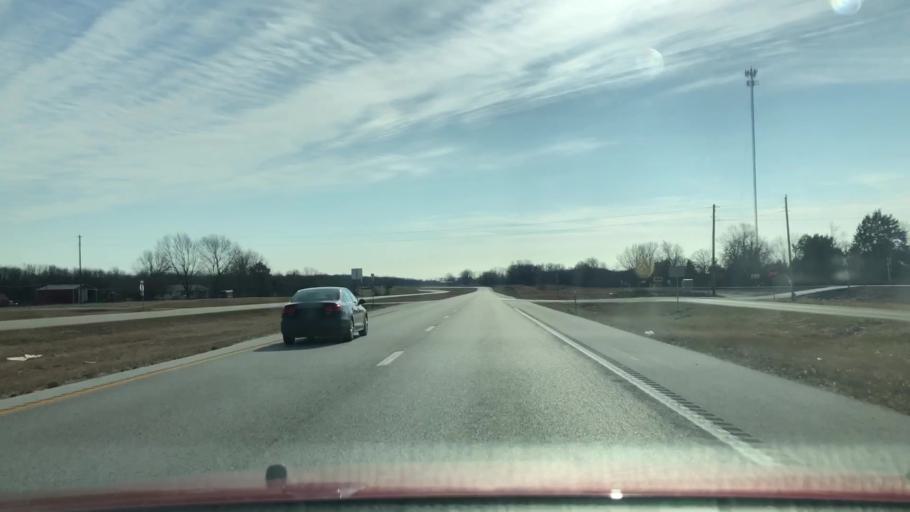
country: US
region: Missouri
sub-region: Webster County
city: Seymour
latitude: 37.1392
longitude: -92.7452
